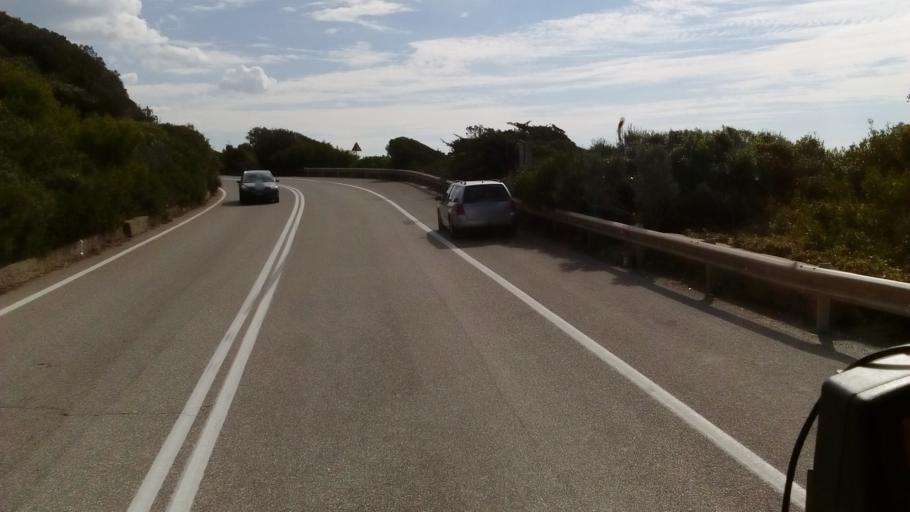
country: IT
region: Tuscany
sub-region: Provincia di Livorno
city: Quercianella
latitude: 43.4700
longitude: 10.3361
